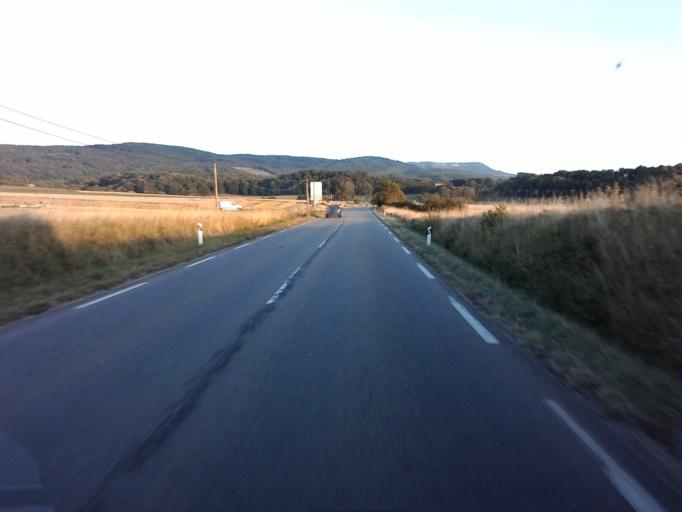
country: FR
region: Franche-Comte
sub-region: Departement du Doubs
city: Quingey
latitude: 47.0646
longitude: 5.8820
